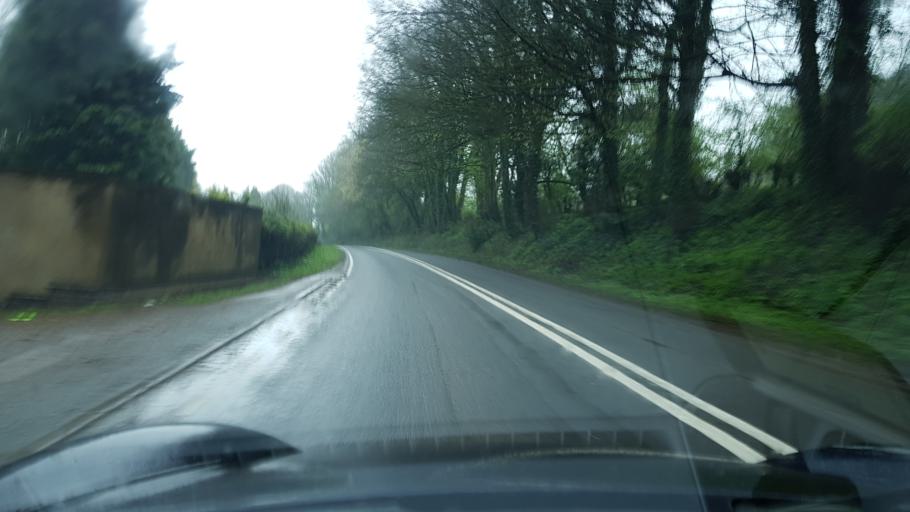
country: GB
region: England
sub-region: Gloucestershire
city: Mitcheldean
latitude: 51.8630
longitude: -2.4771
